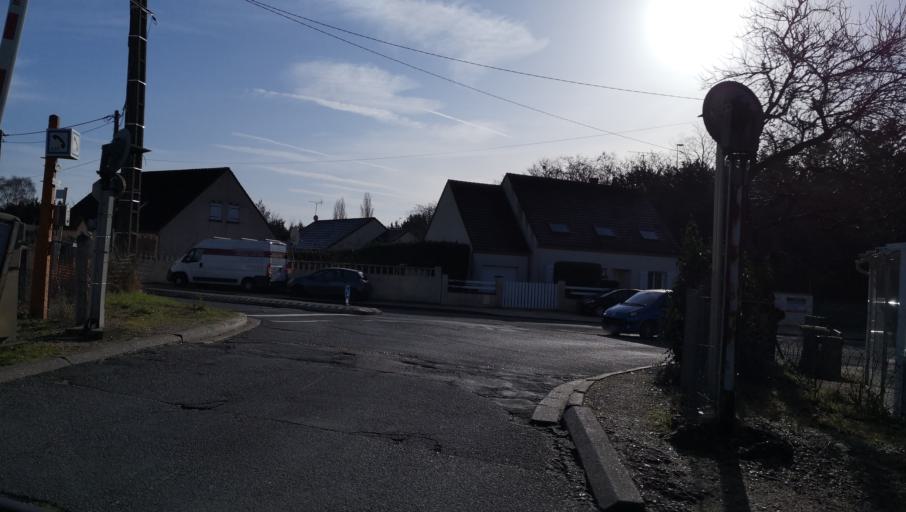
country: FR
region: Centre
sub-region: Departement du Loiret
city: Fleury-les-Aubrais
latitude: 47.9412
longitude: 1.9111
